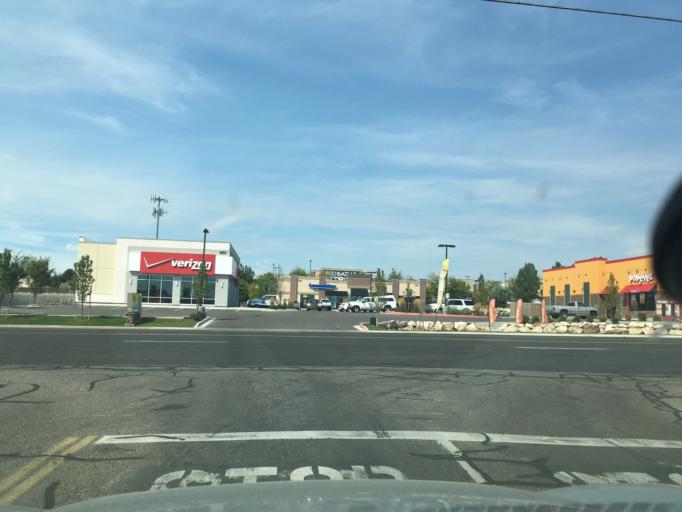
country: US
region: Utah
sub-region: Davis County
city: Hill Air Force Bace
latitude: 41.0890
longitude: -111.9828
